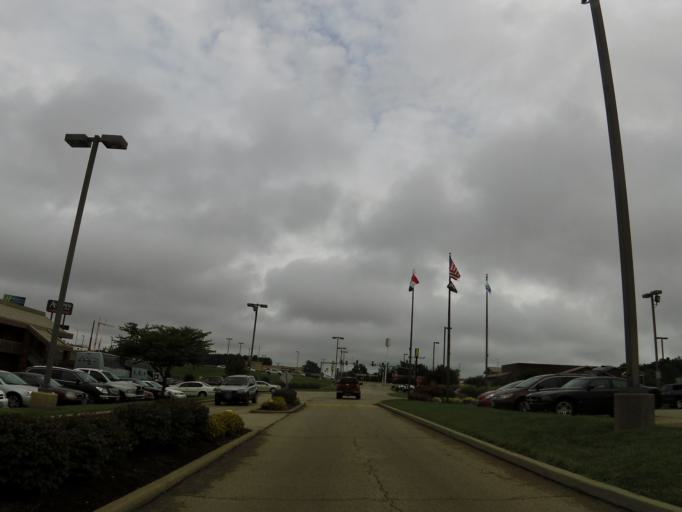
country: US
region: Missouri
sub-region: Cape Girardeau County
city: Cape Girardeau
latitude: 37.3010
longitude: -89.5773
